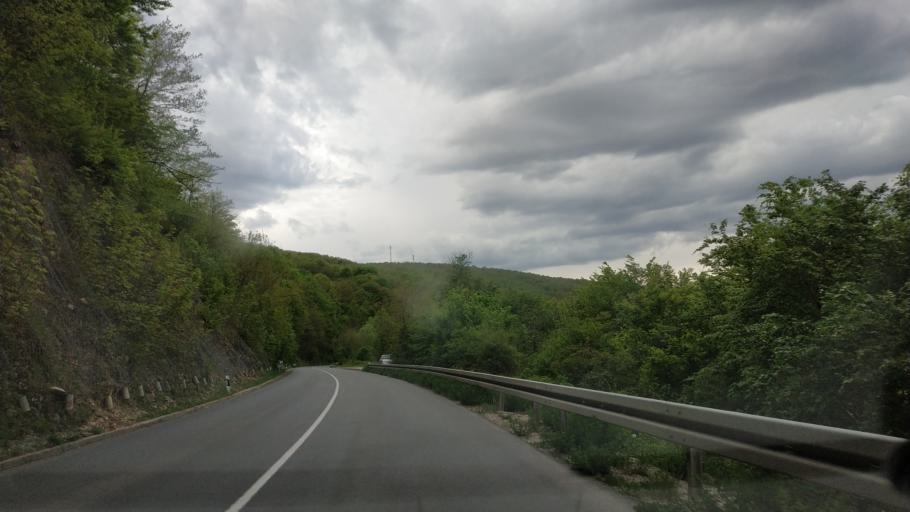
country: RS
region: Central Serbia
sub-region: Nisavski Okrug
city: Aleksinac
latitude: 43.6504
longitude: 21.7374
